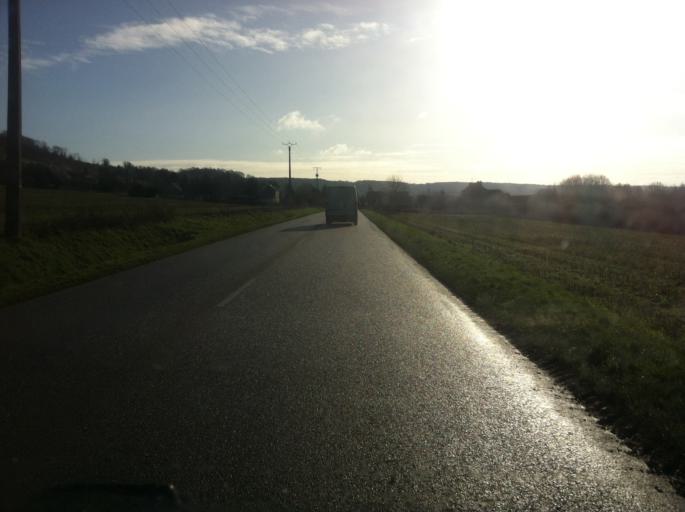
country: FR
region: Haute-Normandie
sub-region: Departement de la Seine-Maritime
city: Henouville
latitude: 49.4631
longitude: 0.9552
